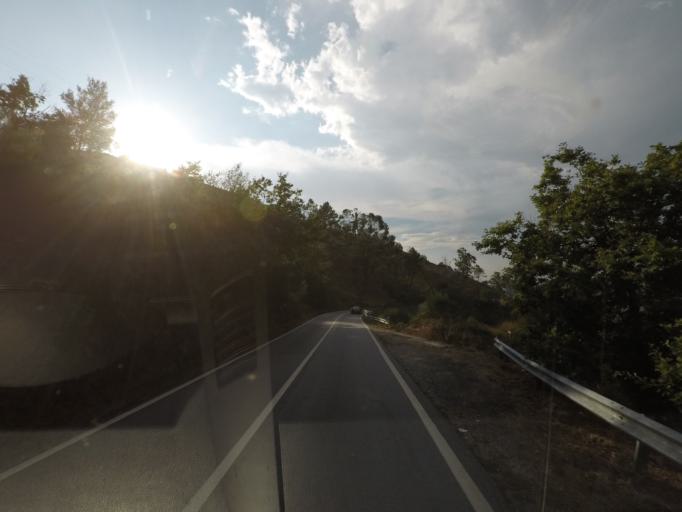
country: PT
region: Porto
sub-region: Baiao
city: Valadares
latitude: 41.1994
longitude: -7.9547
